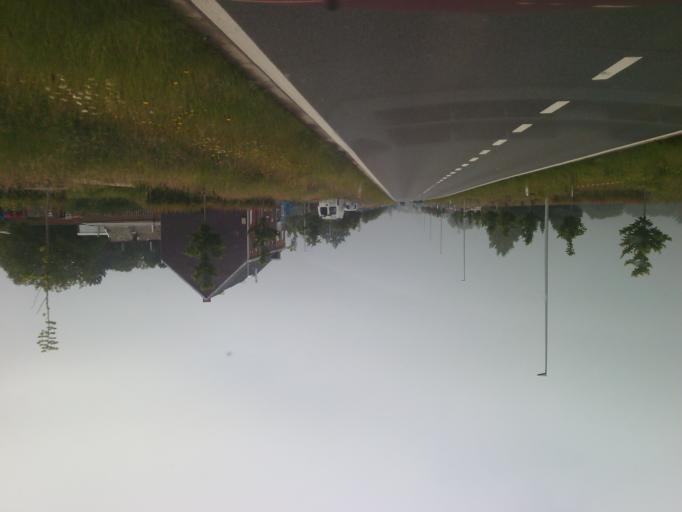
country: BE
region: Flanders
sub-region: Provincie Oost-Vlaanderen
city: Aalst
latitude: 50.9710
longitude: 4.0414
